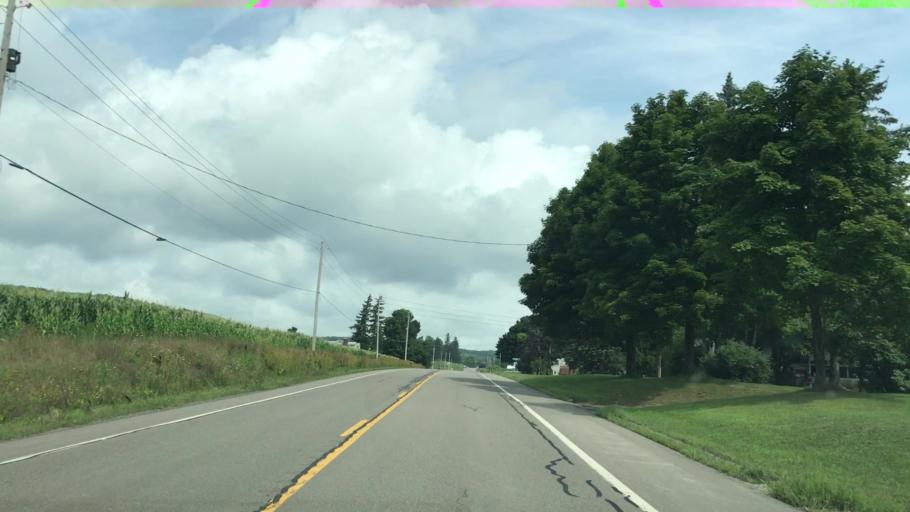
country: US
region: New York
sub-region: Ontario County
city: Naples
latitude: 42.5088
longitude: -77.2866
